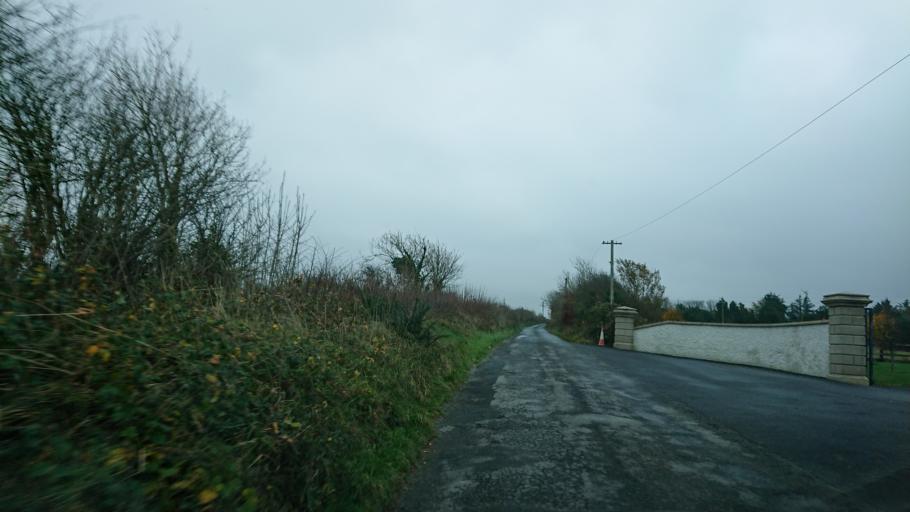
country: IE
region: Munster
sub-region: Waterford
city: Dunmore East
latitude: 52.1983
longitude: -7.0093
